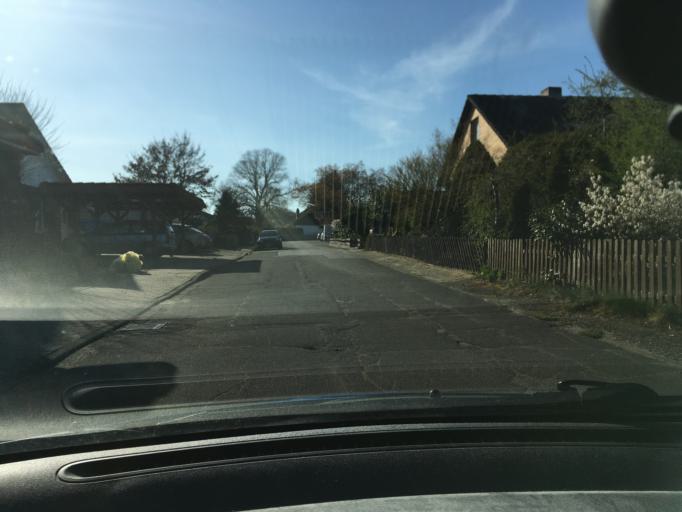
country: DE
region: Lower Saxony
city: Amelinghausen
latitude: 53.1245
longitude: 10.2186
